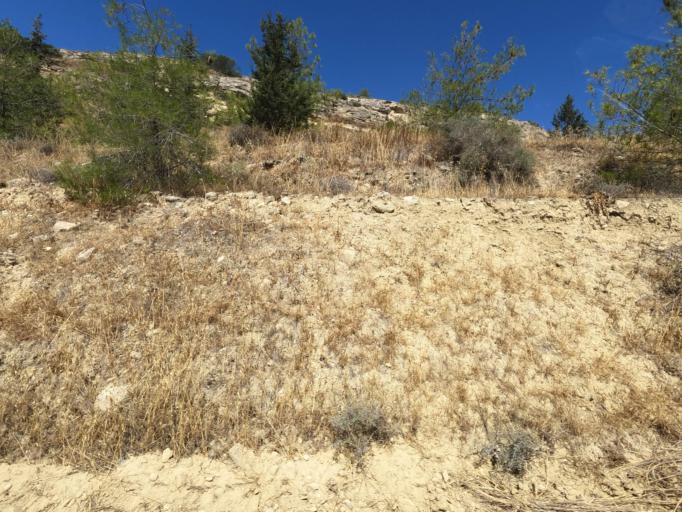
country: CY
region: Larnaka
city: Voroklini
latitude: 34.9940
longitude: 33.6478
